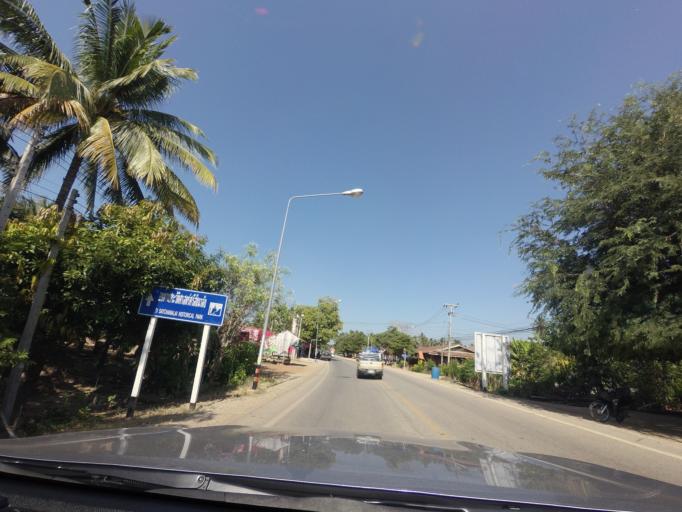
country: TH
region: Sukhothai
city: Sawankhalok
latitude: 17.4011
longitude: 99.7982
